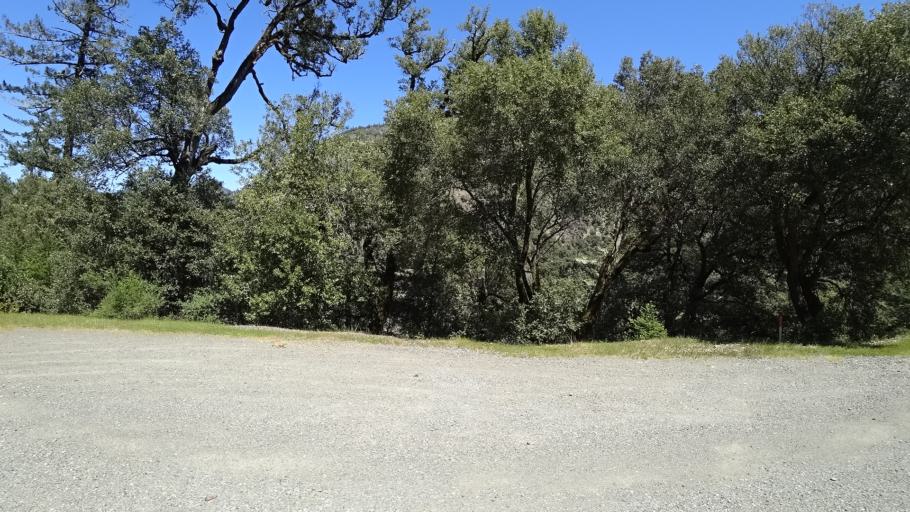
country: US
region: California
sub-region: Humboldt County
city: Willow Creek
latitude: 40.8179
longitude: -123.4793
